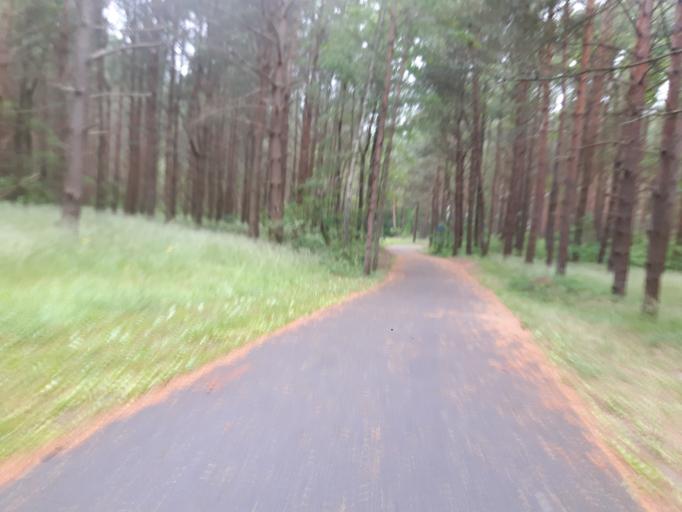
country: LT
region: Klaipedos apskritis
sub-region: Klaipeda
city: Palanga
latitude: 55.8844
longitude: 21.0591
